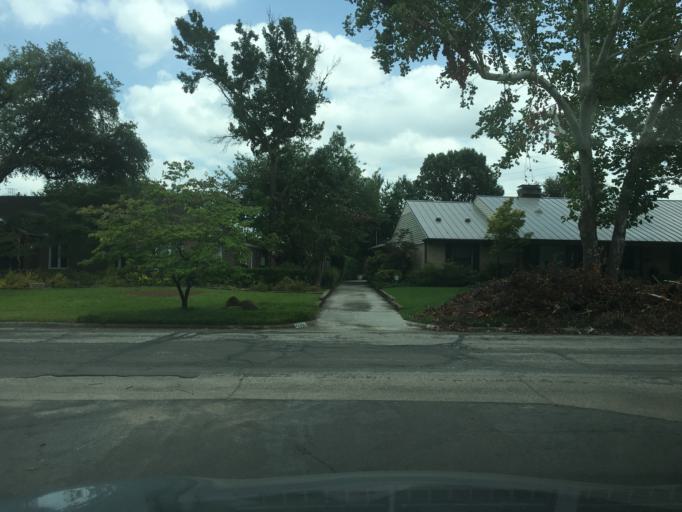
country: US
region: Texas
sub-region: Dallas County
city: Addison
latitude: 32.9040
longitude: -96.8242
